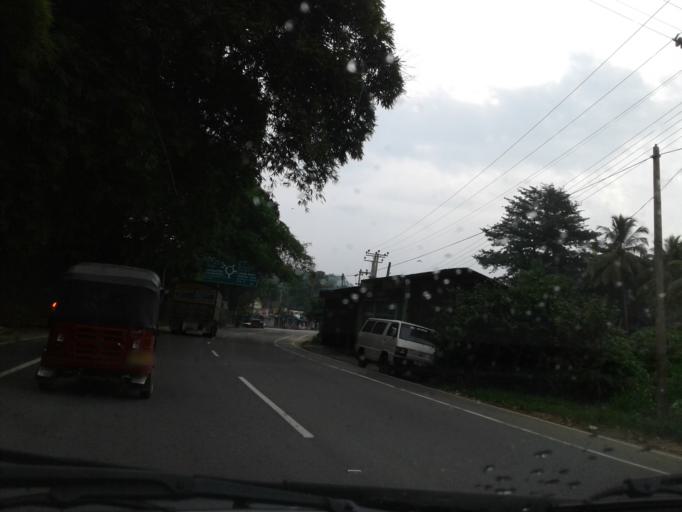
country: LK
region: Central
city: Kadugannawa
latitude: 7.2482
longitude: 80.3455
